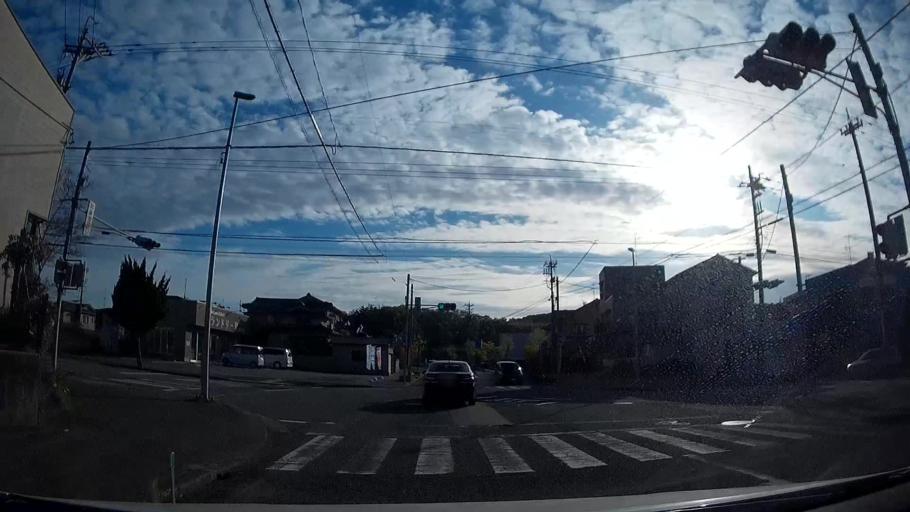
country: JP
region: Ishikawa
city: Nanao
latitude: 37.0822
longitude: 136.9230
